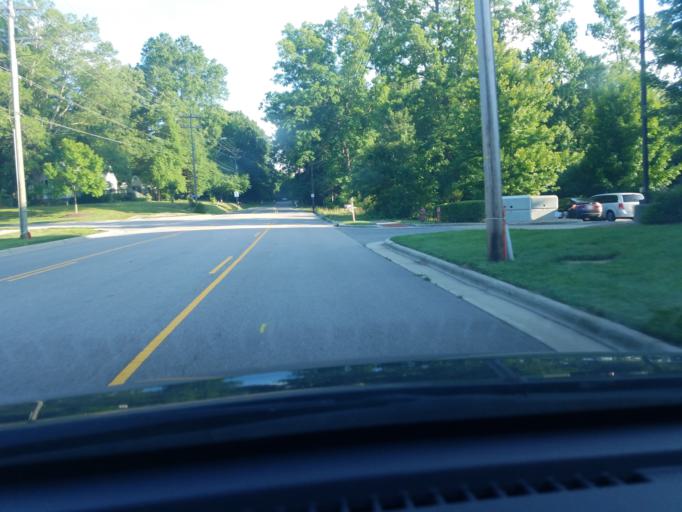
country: US
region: North Carolina
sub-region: Orange County
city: Chapel Hill
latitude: 35.9489
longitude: -78.9945
